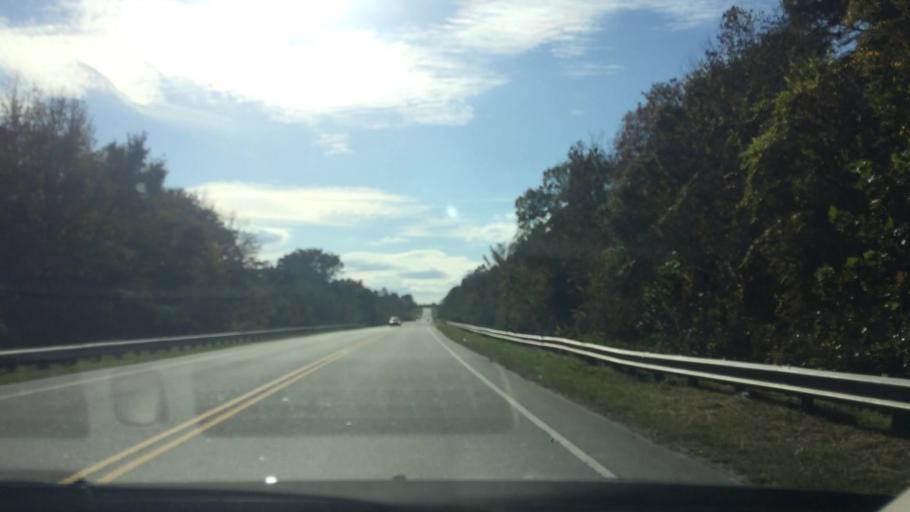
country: US
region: North Carolina
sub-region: Greene County
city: Snow Hill
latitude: 35.4595
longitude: -77.6737
